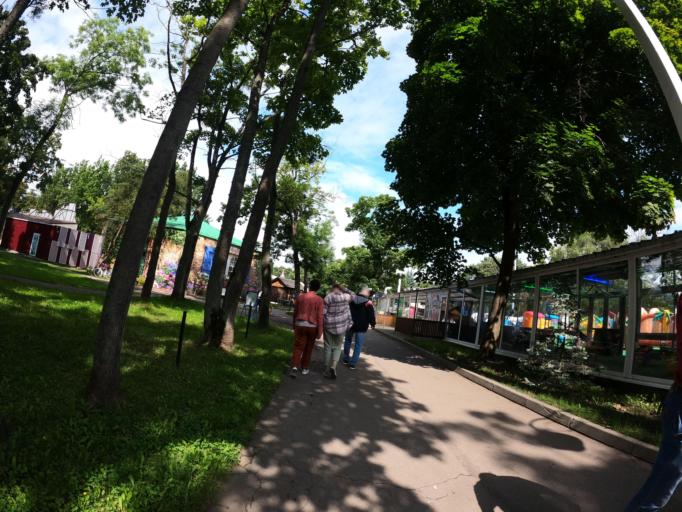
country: RU
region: Kaliningrad
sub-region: Gorod Kaliningrad
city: Kaliningrad
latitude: 54.7172
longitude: 20.4762
